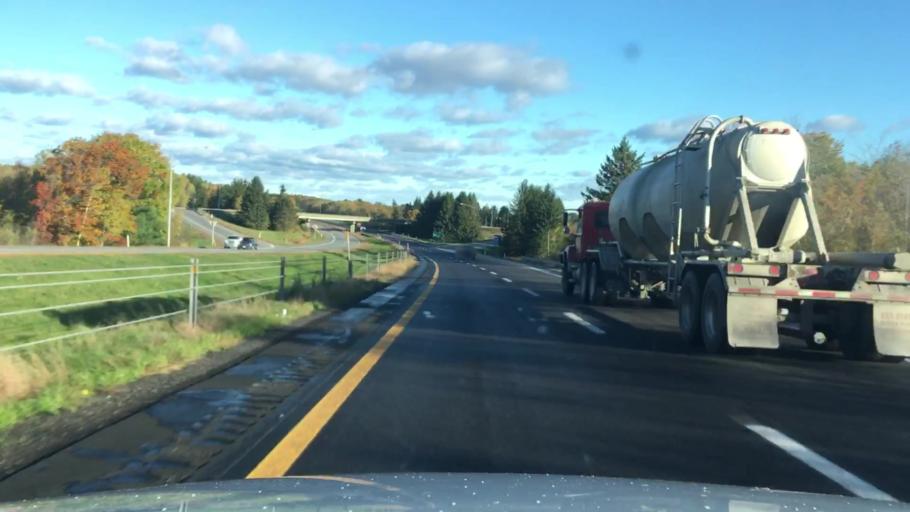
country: US
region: Maine
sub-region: Penobscot County
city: Orono
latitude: 44.8993
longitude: -68.6907
